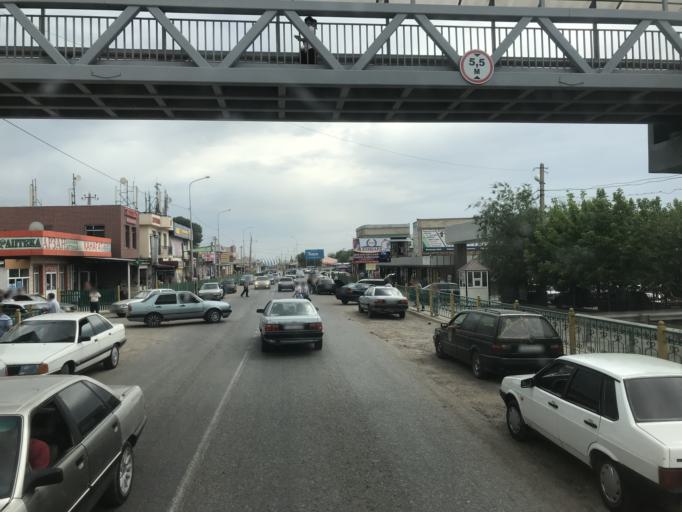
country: KZ
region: Ongtustik Qazaqstan
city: Saryaghash
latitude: 41.3397
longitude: 68.9519
